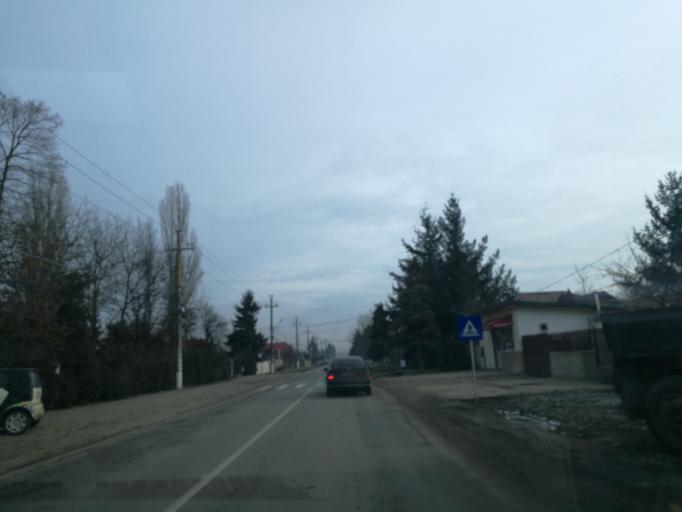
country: RO
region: Ilfov
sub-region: Comuna Moara Vlasiei
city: Moara Vlasiei
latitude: 44.6406
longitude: 26.2068
